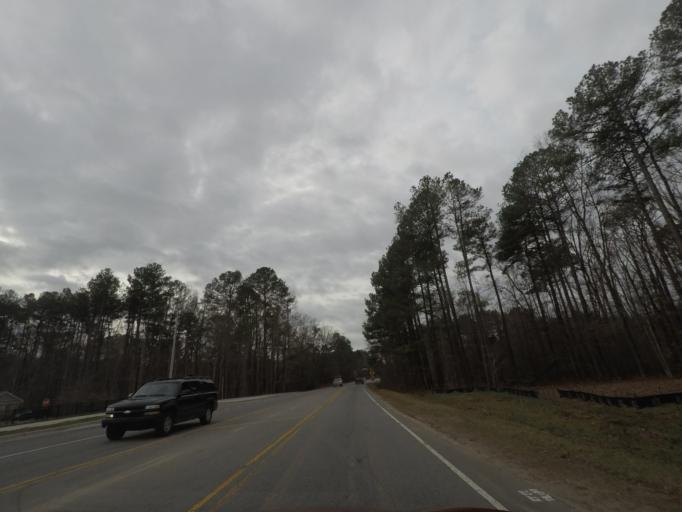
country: US
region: North Carolina
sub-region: Wake County
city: Morrisville
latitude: 35.8325
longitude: -78.8149
